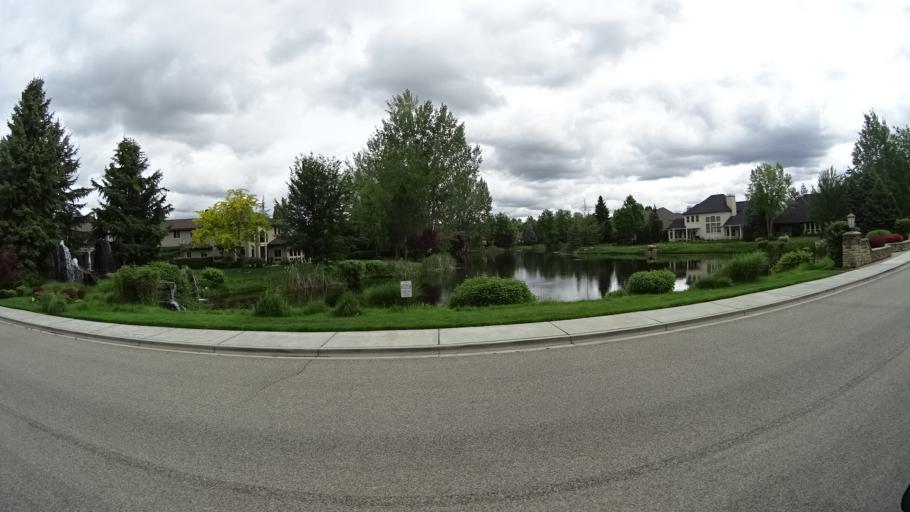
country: US
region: Idaho
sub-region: Ada County
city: Eagle
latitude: 43.6823
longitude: -116.3578
